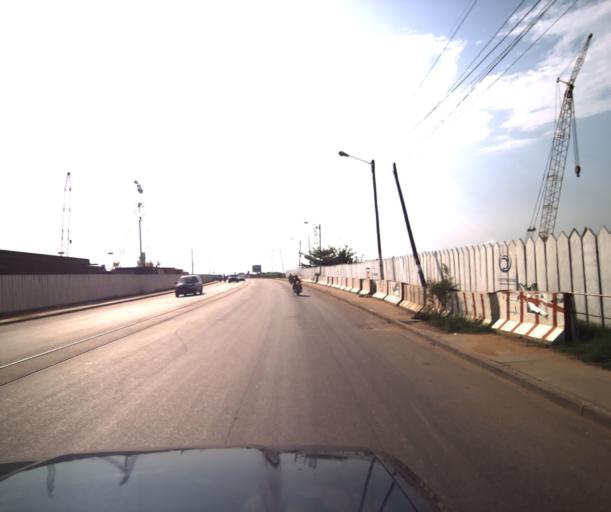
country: CM
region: Littoral
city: Bonaberi
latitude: 4.0723
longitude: 9.6979
